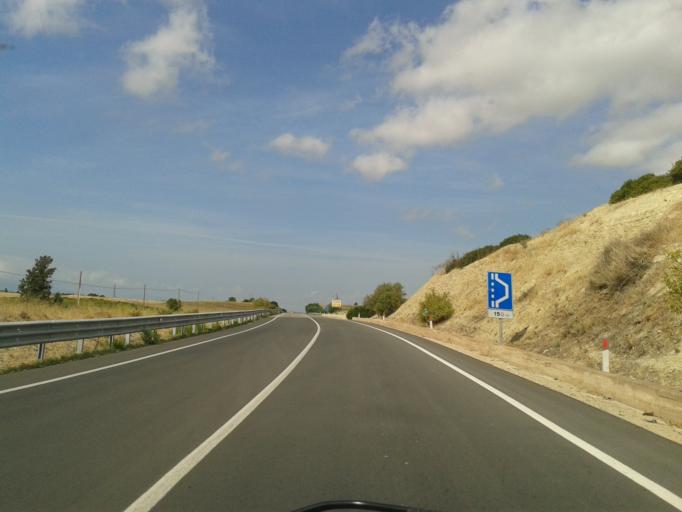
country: IT
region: Sardinia
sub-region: Provincia di Cagliari
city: Maracalagonis
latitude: 39.2687
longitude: 9.2129
